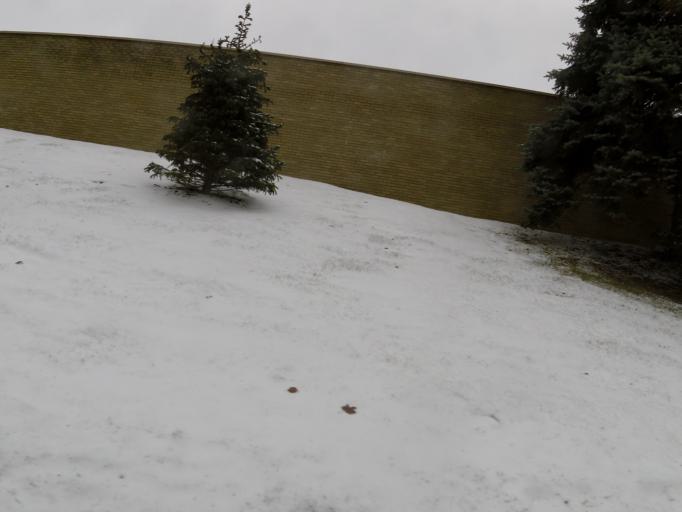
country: US
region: Minnesota
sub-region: Hennepin County
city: Eden Prairie
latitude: 44.8559
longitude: -93.4270
